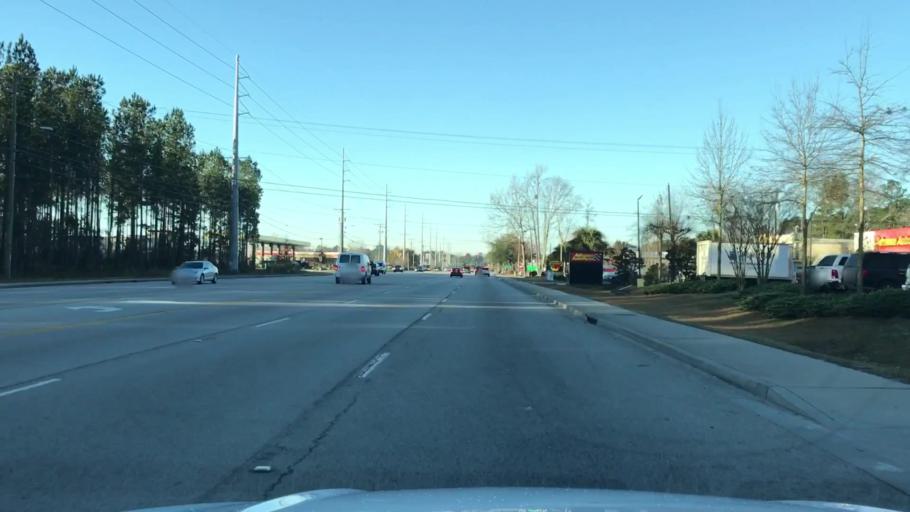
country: US
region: South Carolina
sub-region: Berkeley County
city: Ladson
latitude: 32.9203
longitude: -80.1002
